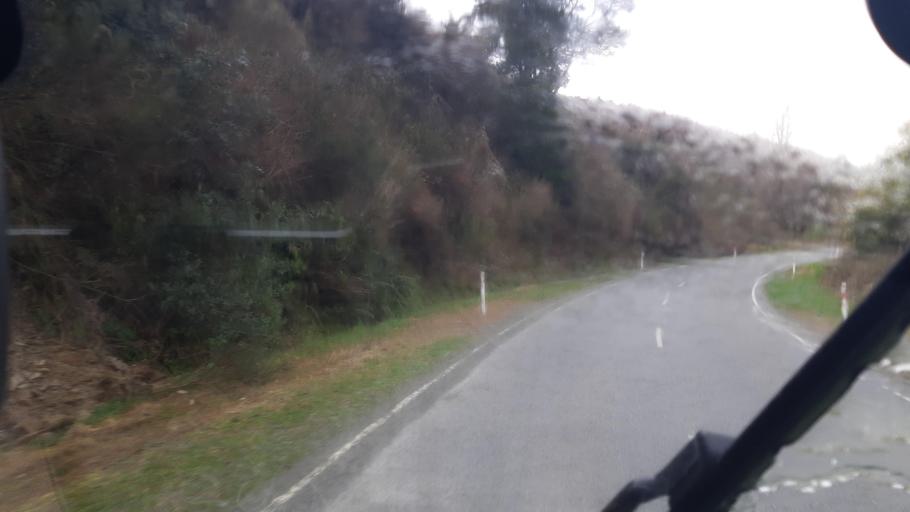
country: NZ
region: Tasman
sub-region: Tasman District
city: Motueka
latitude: -41.2657
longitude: 172.8316
